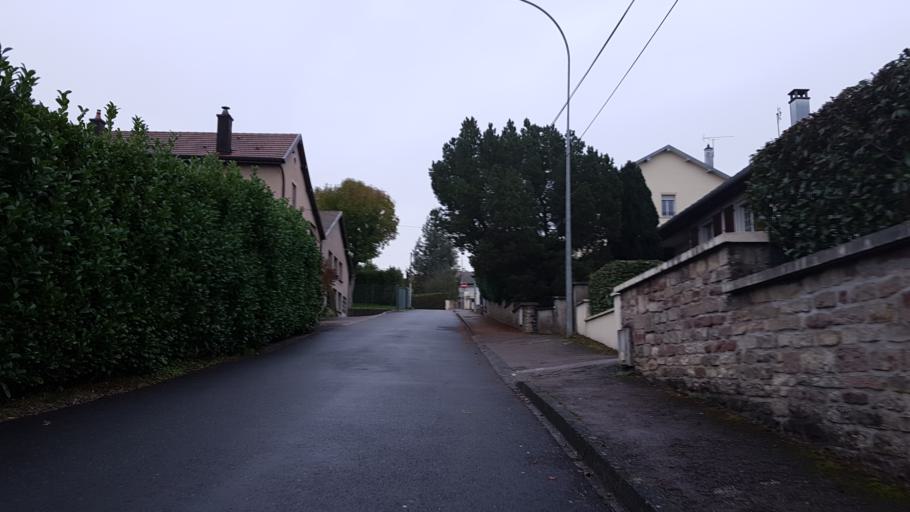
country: FR
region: Franche-Comte
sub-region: Departement de la Haute-Saone
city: Luxeuil-les-Bains
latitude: 47.8236
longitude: 6.3760
